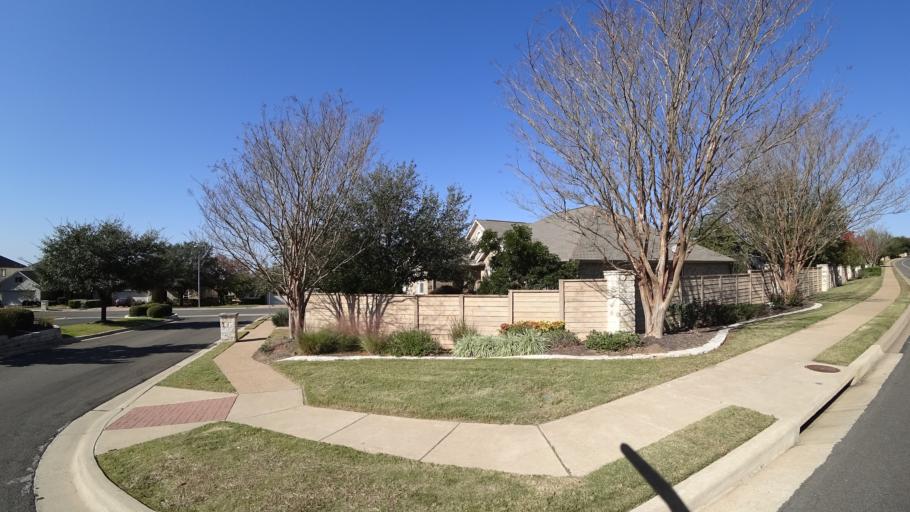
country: US
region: Texas
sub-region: Williamson County
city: Anderson Mill
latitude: 30.3844
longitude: -97.8509
